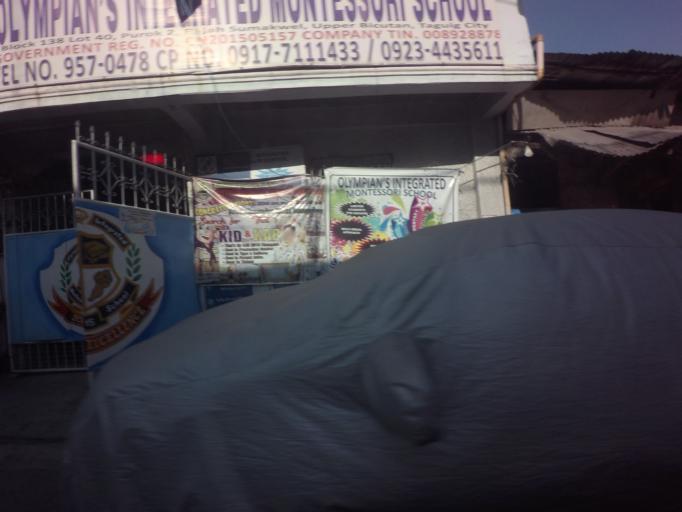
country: PH
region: Calabarzon
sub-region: Province of Rizal
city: Taguig
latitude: 14.4960
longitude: 121.0478
